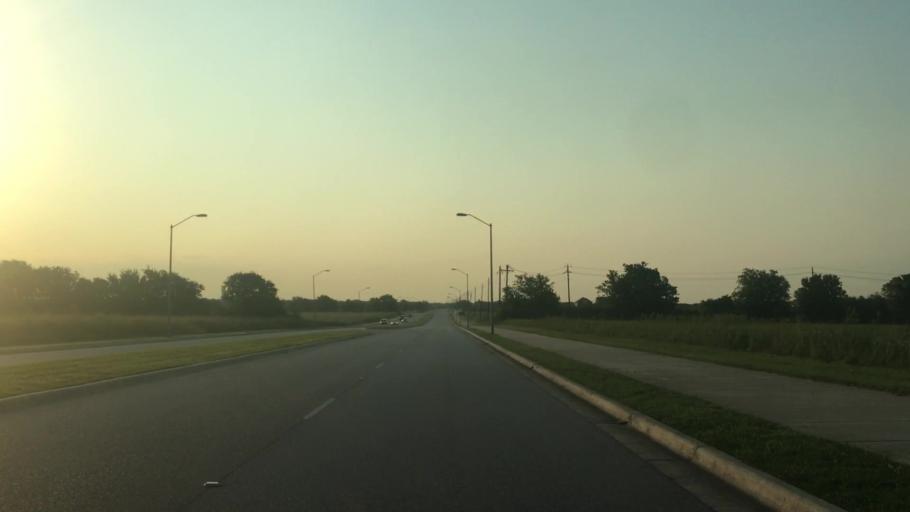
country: US
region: Texas
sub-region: Travis County
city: Windemere
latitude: 30.4767
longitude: -97.6625
